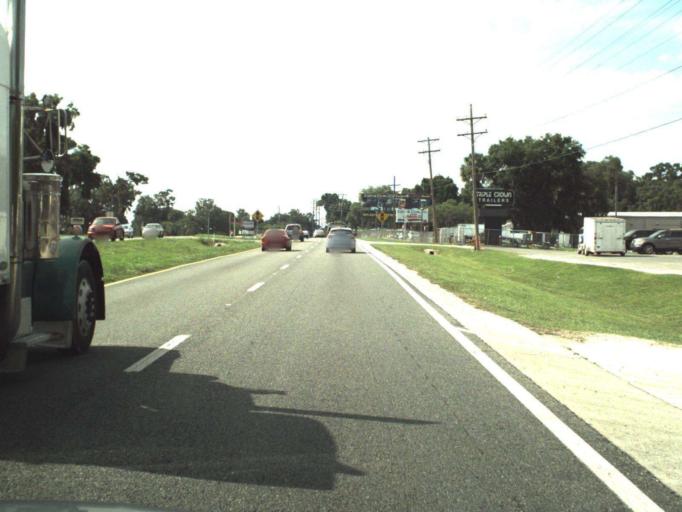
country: US
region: Florida
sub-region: Marion County
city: Ocala
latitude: 29.1449
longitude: -82.1132
